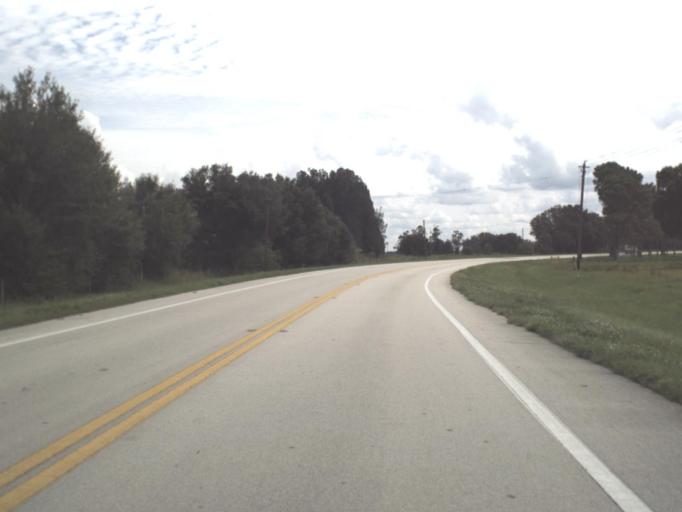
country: US
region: Florida
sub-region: DeSoto County
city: Southeast Arcadia
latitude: 27.1402
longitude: -81.7977
